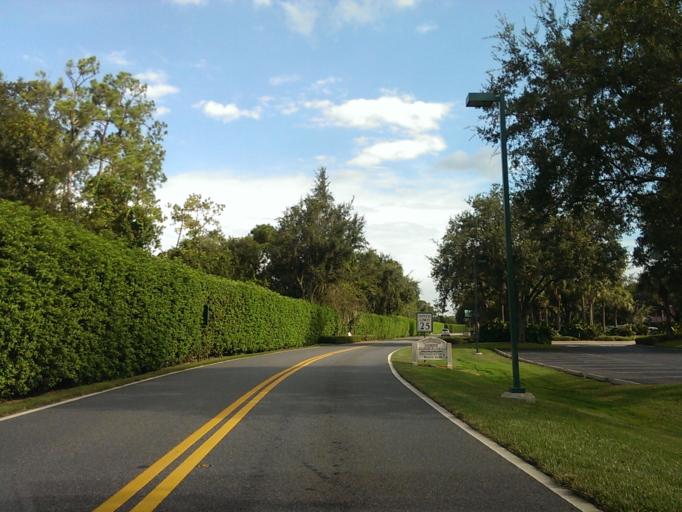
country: US
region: Florida
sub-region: Osceola County
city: Celebration
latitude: 28.3614
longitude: -81.5413
